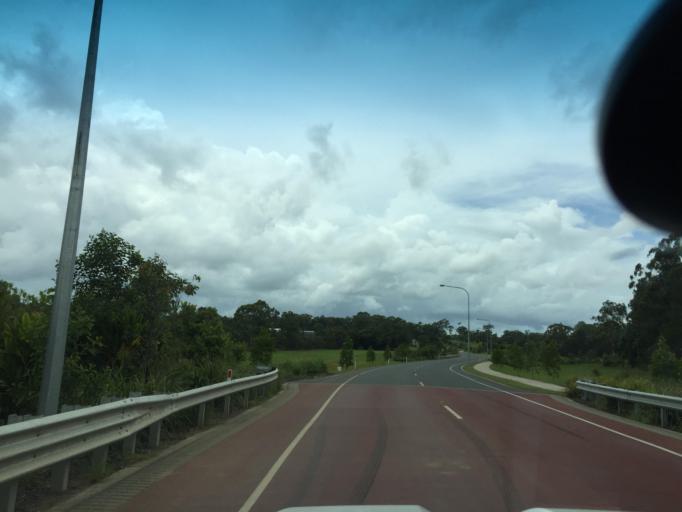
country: AU
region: Queensland
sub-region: Moreton Bay
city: Caboolture
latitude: -27.0600
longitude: 152.9343
